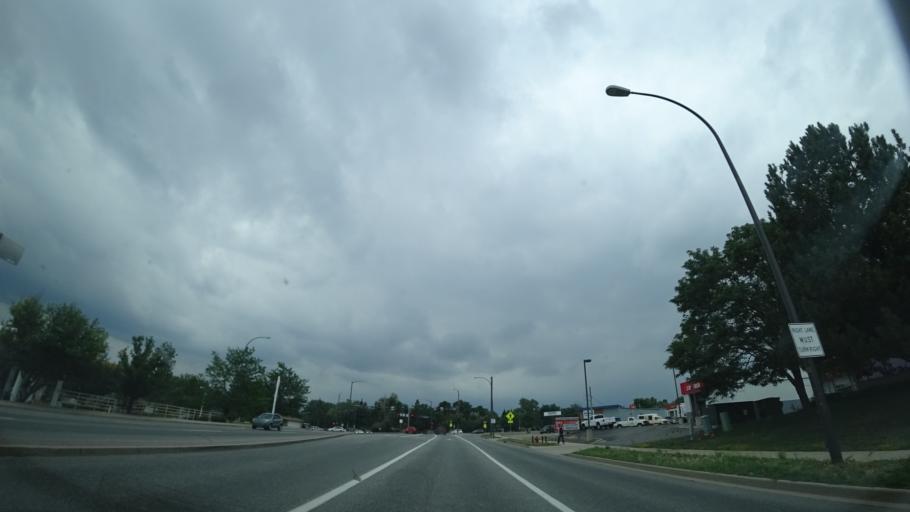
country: US
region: Colorado
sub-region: Jefferson County
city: West Pleasant View
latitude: 39.7107
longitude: -105.1332
